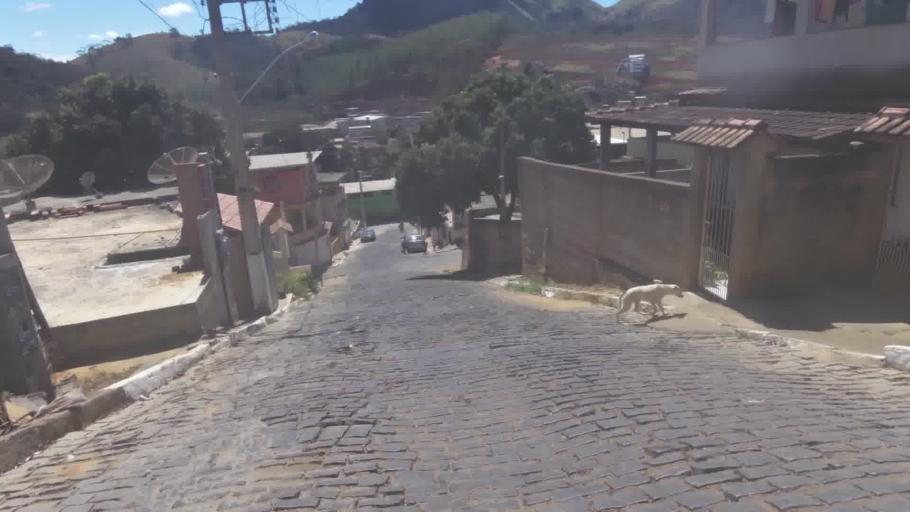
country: BR
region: Espirito Santo
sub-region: Cachoeiro De Itapemirim
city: Cachoeiro de Itapemirim
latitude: -20.9169
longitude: -41.1965
